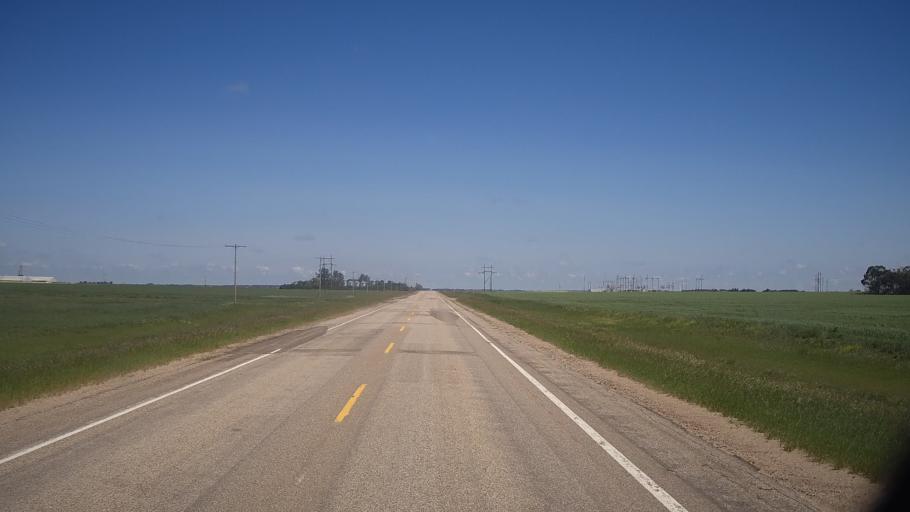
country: CA
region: Saskatchewan
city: Saskatoon
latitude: 51.9746
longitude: -106.0753
